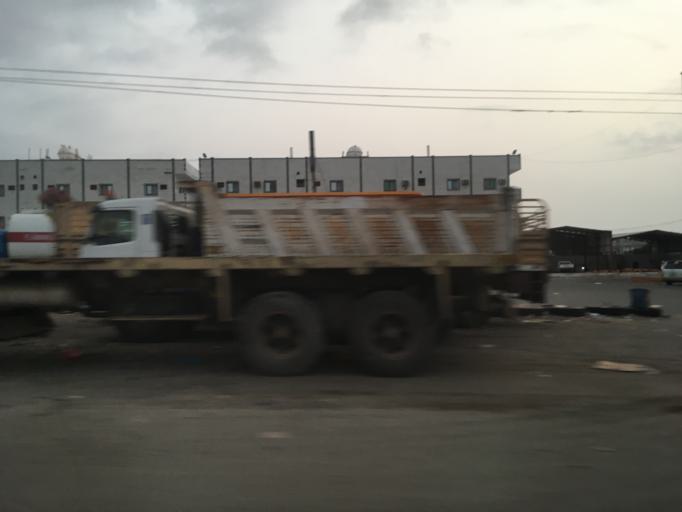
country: YE
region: Lahij
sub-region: Al  Hawtah
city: Lahij
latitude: 13.0063
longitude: 44.9103
